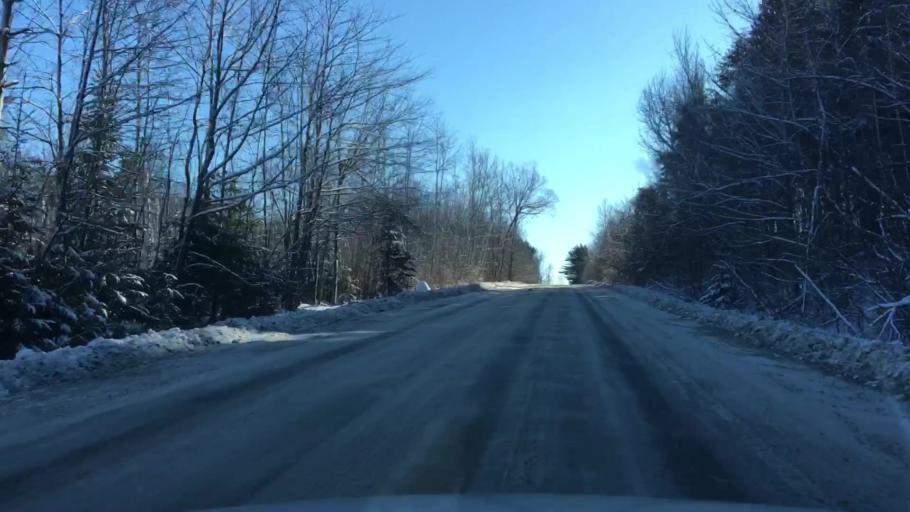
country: US
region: Maine
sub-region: Kennebec County
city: Winthrop
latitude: 44.3475
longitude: -69.9901
